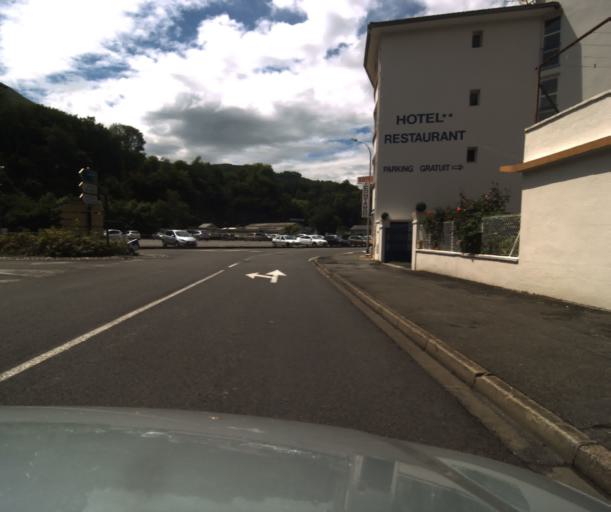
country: FR
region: Midi-Pyrenees
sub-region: Departement des Hautes-Pyrenees
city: Lourdes
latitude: 43.0899
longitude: -0.0534
